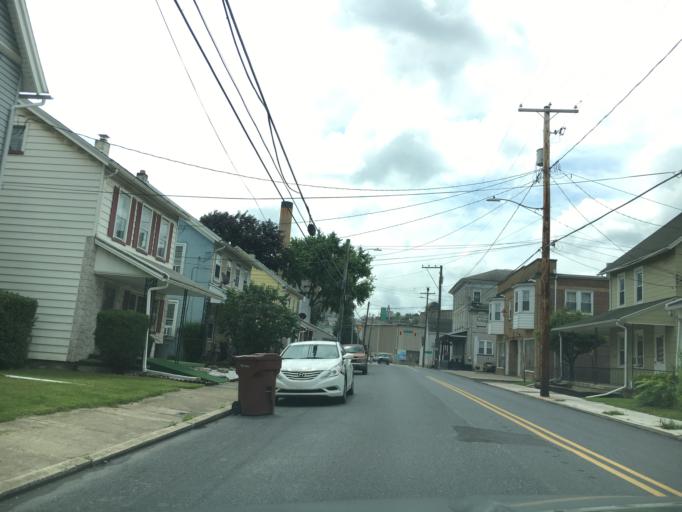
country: US
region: Pennsylvania
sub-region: Lehigh County
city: Cementon
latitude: 40.6900
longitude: -75.5082
